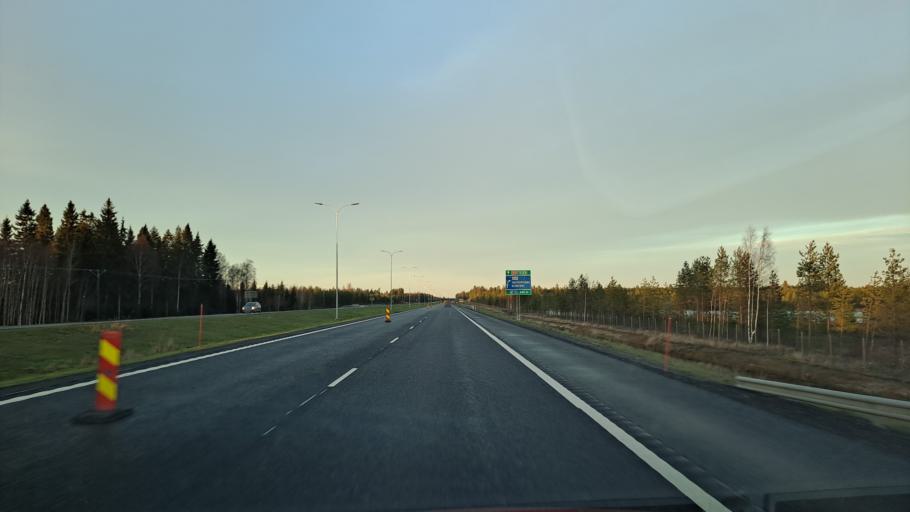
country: FI
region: Northern Ostrobothnia
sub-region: Oulu
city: Haukipudas
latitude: 65.1502
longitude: 25.4316
